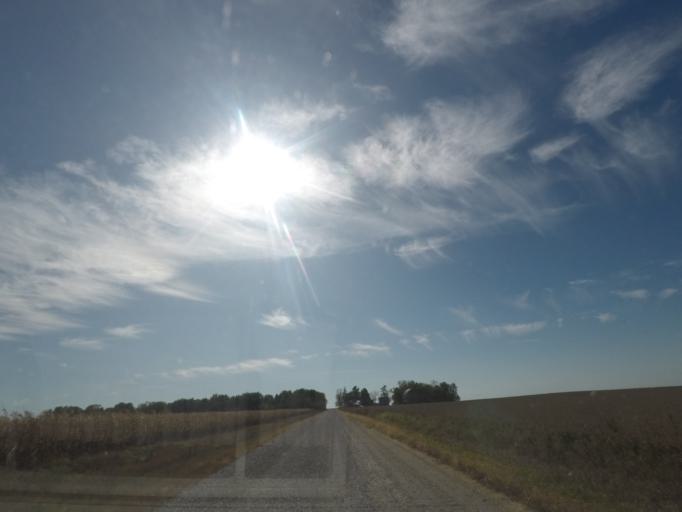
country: US
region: Iowa
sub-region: Story County
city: Nevada
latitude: 42.0526
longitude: -93.3290
